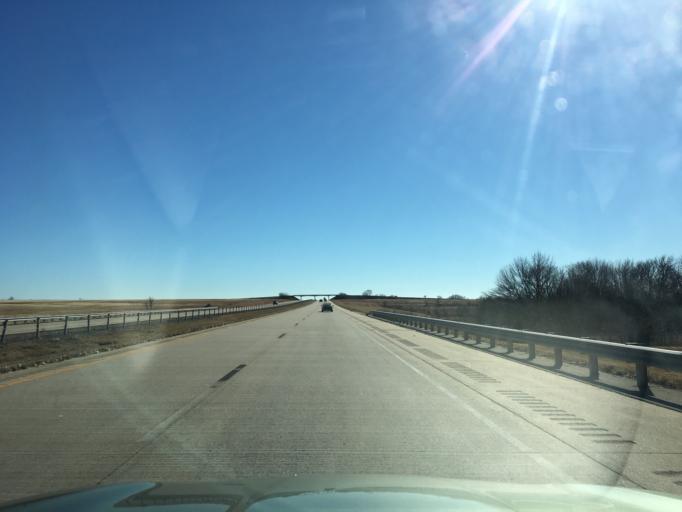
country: US
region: Oklahoma
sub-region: Kay County
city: Tonkawa
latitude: 36.4987
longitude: -97.3336
